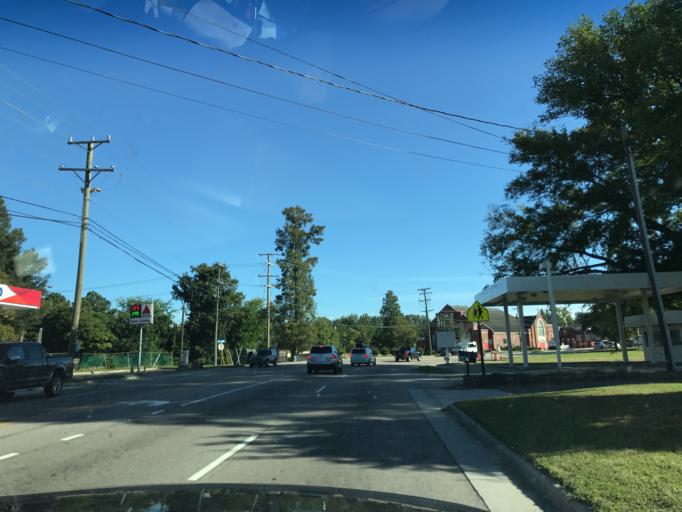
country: US
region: Virginia
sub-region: City of Portsmouth
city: Portsmouth Heights
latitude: 36.7445
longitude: -76.3454
